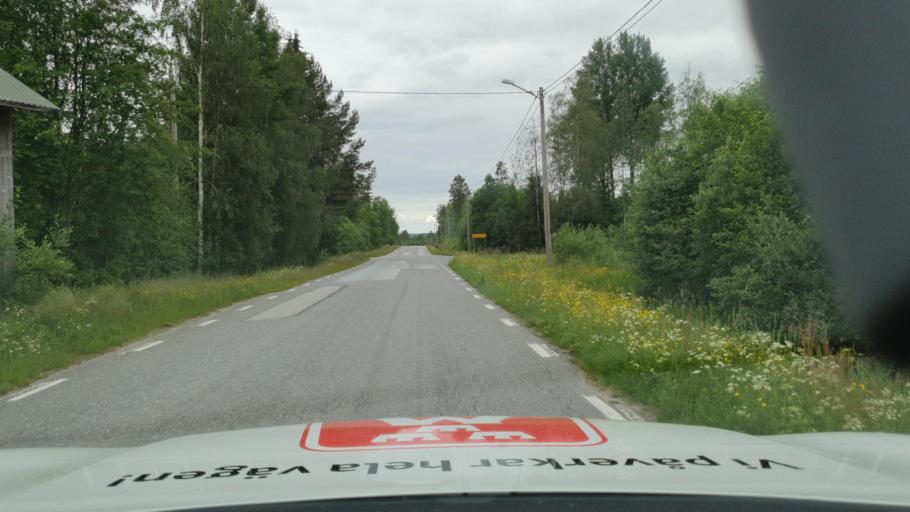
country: SE
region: Vaesterbotten
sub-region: Nordmalings Kommun
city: Nordmaling
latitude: 63.5274
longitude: 19.4117
